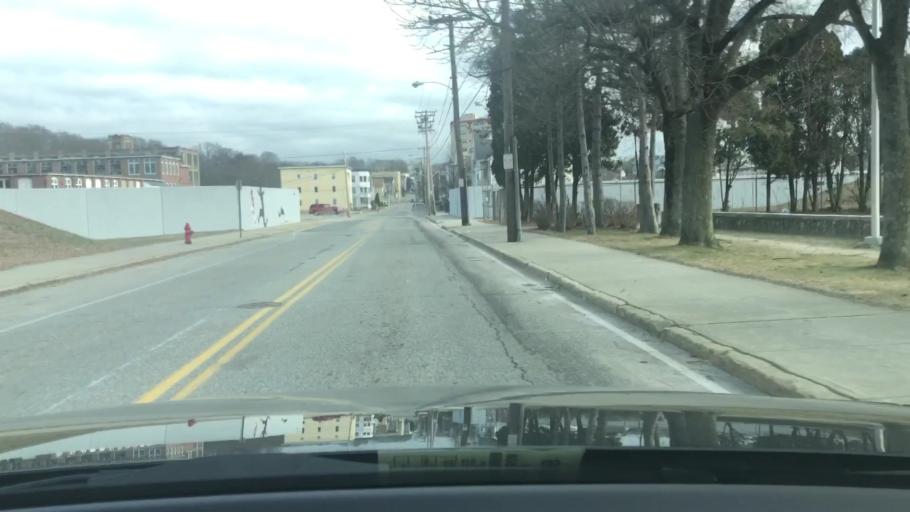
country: US
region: Rhode Island
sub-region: Providence County
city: Woonsocket
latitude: 42.0108
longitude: -71.5098
